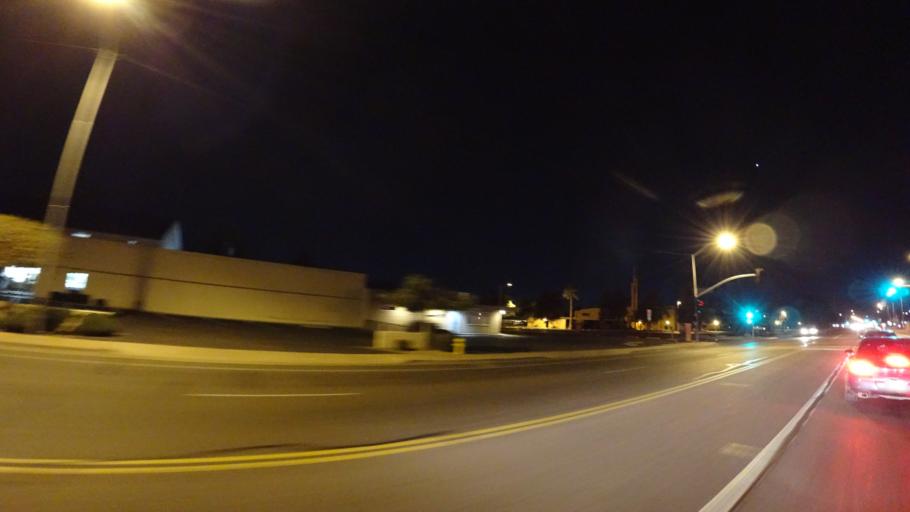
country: US
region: Arizona
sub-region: Maricopa County
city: Mesa
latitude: 33.4225
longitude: -111.8005
